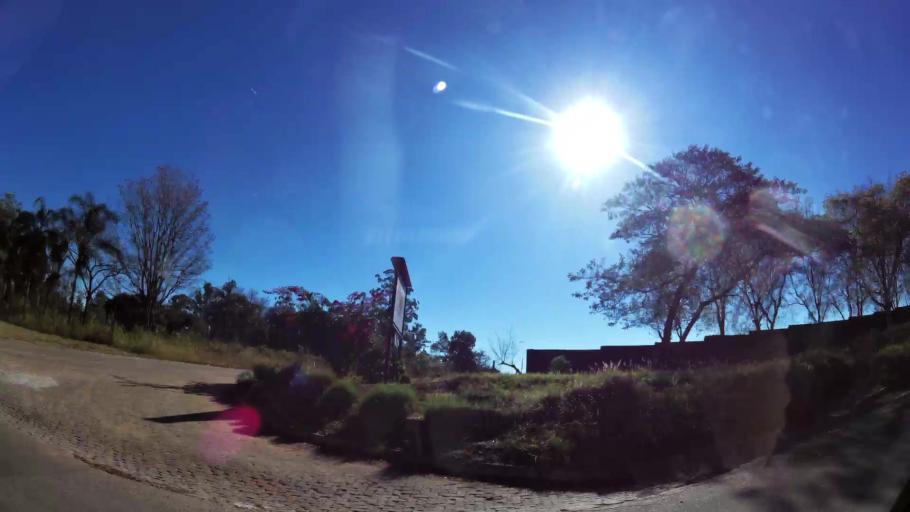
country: ZA
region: Limpopo
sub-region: Mopani District Municipality
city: Tzaneen
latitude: -23.8364
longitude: 30.1804
